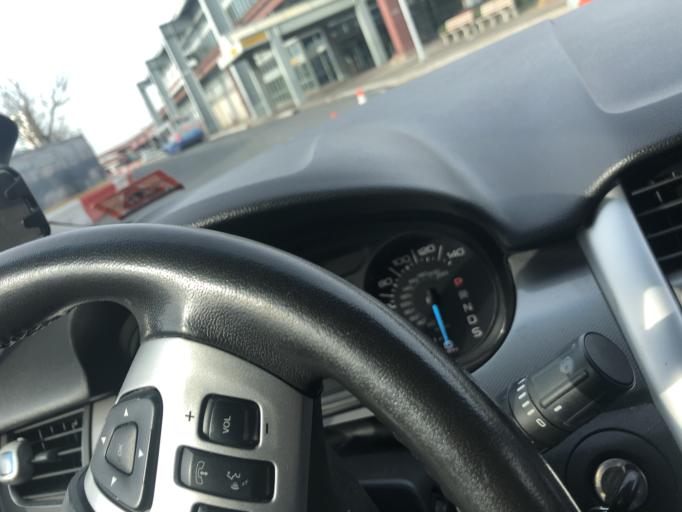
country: US
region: New Jersey
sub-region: Union County
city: Elizabeth
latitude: 40.6896
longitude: -74.1865
